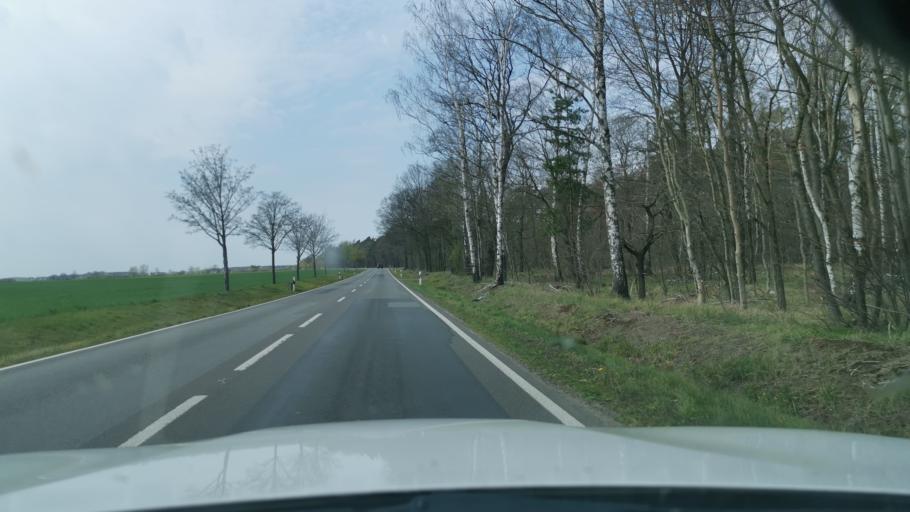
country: DE
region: Saxony
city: Lobnitz
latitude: 51.5607
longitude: 12.4964
